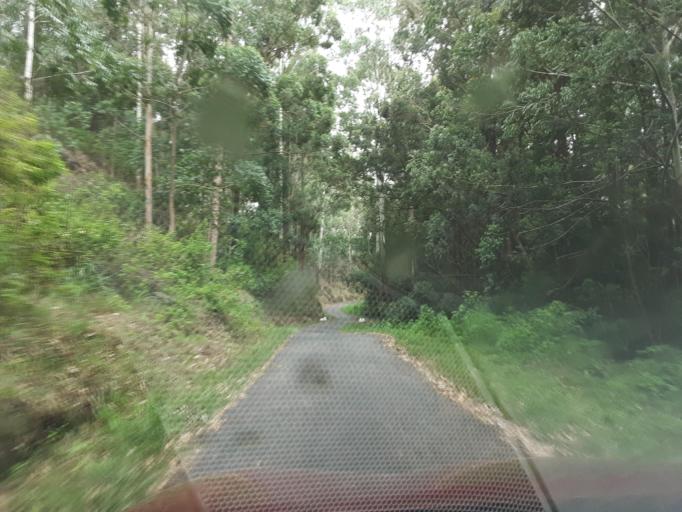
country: LK
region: Uva
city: Haputale
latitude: 6.8132
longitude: 80.8805
